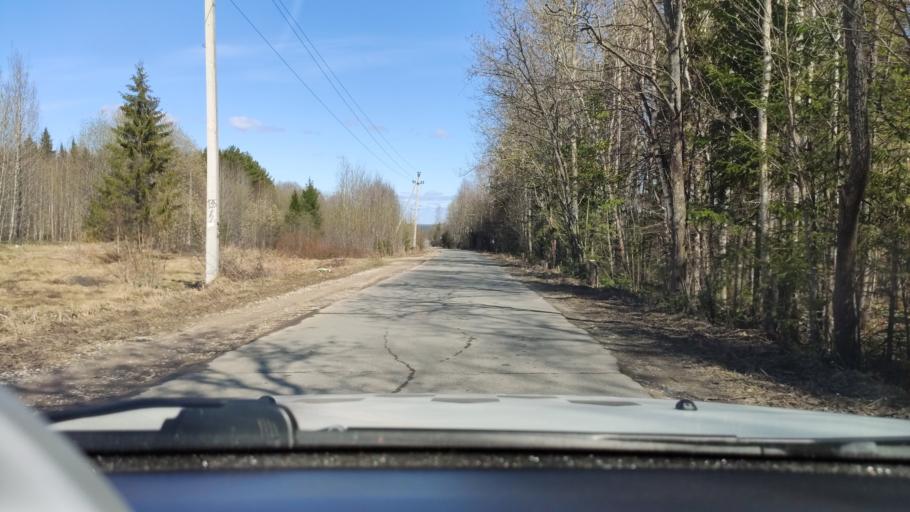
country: RU
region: Perm
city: Novyye Lyady
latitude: 58.0437
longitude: 56.6342
